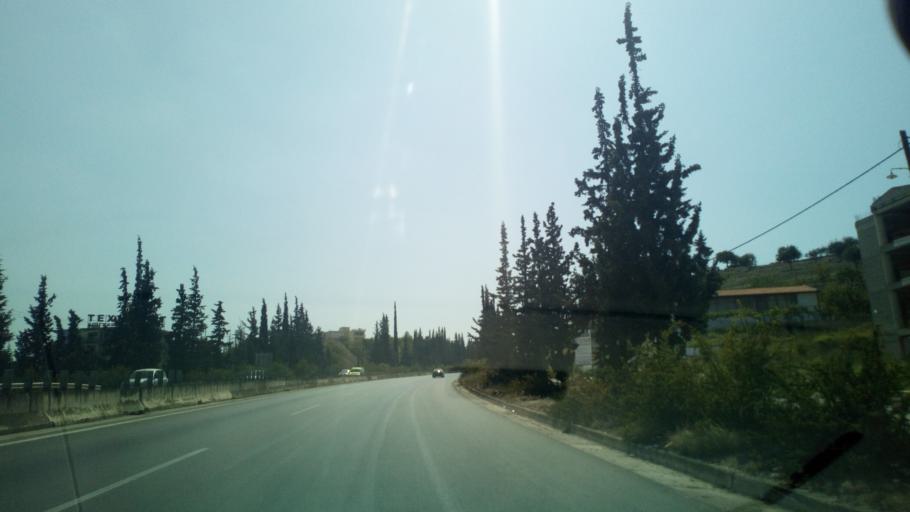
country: GR
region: Central Macedonia
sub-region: Nomos Thessalonikis
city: Neo Rysi
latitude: 40.4875
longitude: 22.9972
